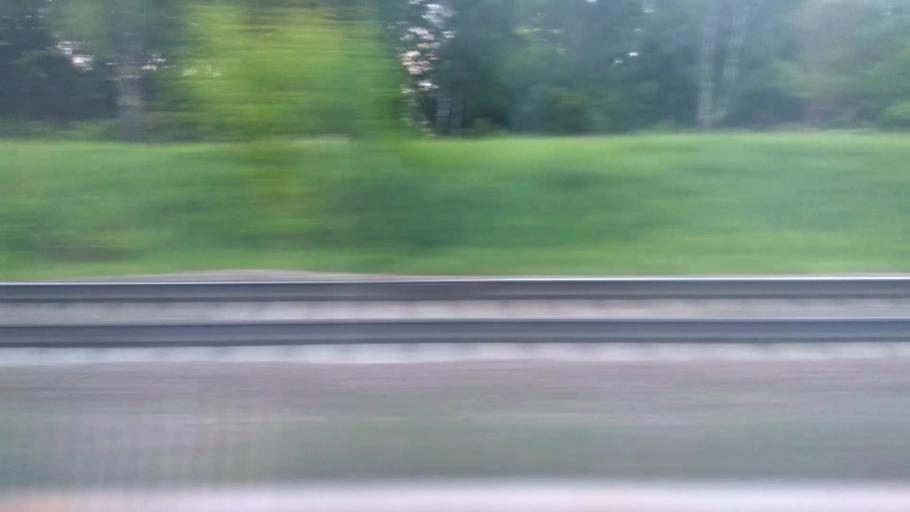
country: RU
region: Moskovskaya
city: Vostryakovo
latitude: 55.3767
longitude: 37.8189
